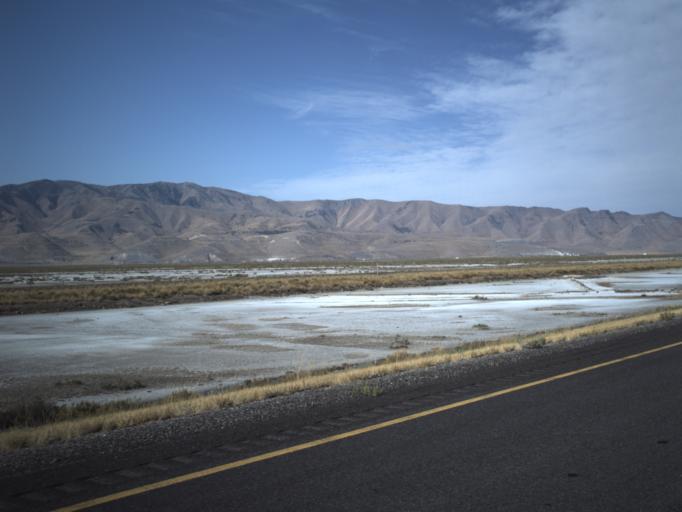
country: US
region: Utah
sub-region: Tooele County
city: Grantsville
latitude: 40.6966
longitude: -112.4765
